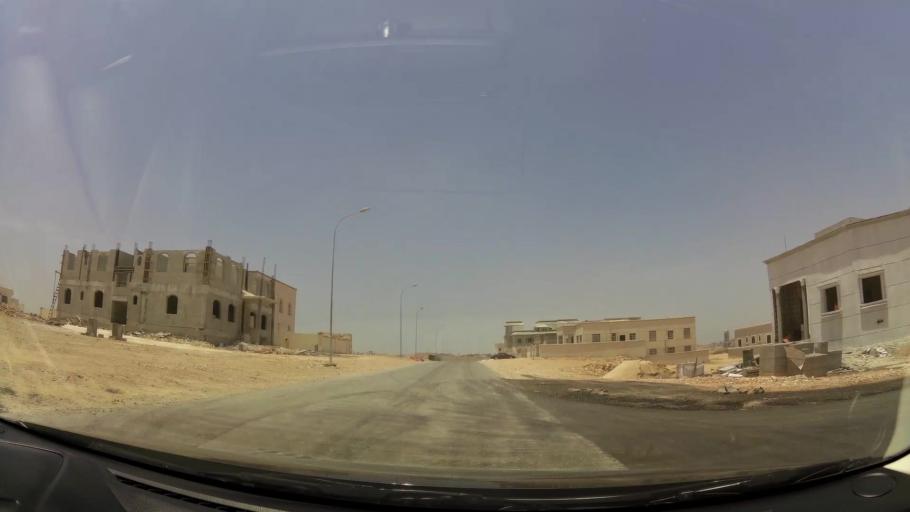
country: OM
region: Zufar
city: Salalah
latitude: 17.0925
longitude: 54.1637
